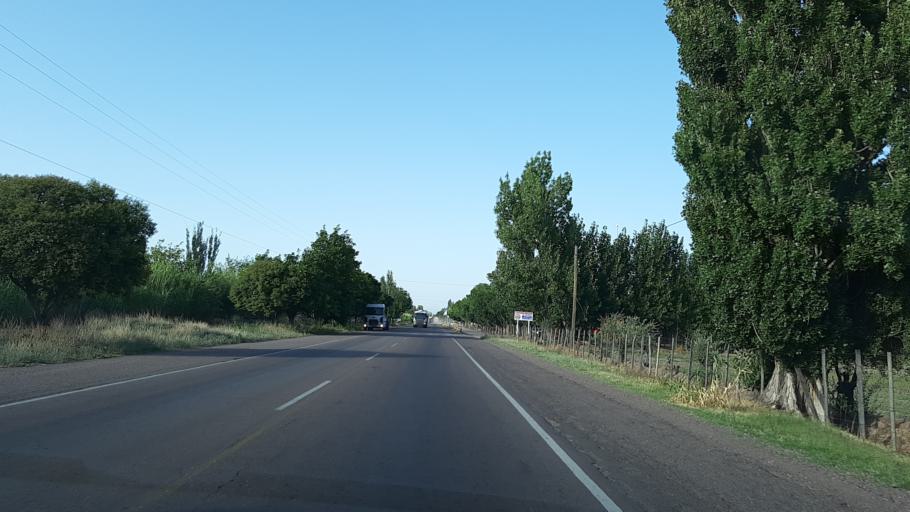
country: AR
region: Mendoza
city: San Martin
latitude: -32.9833
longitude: -68.4622
